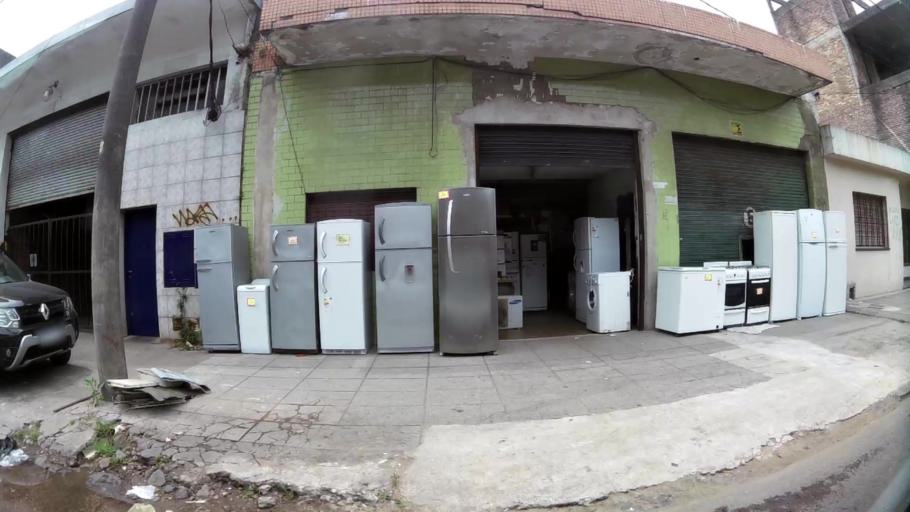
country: AR
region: Buenos Aires
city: San Justo
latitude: -34.6673
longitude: -58.5318
